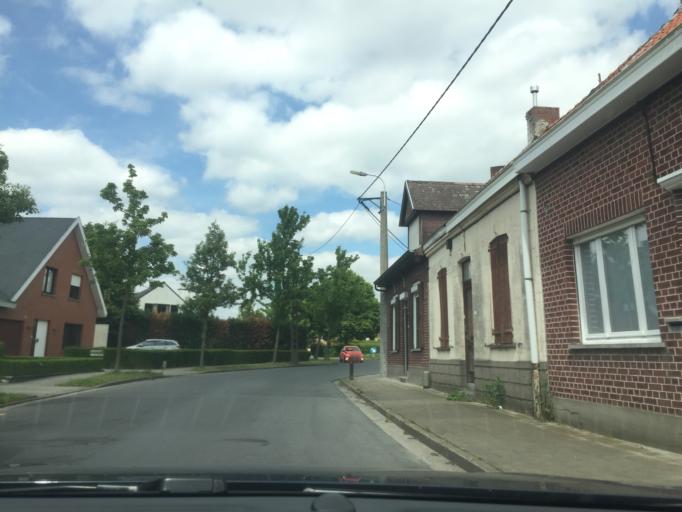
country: BE
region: Flanders
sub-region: Provincie West-Vlaanderen
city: Zwevegem
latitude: 50.8097
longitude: 3.3285
